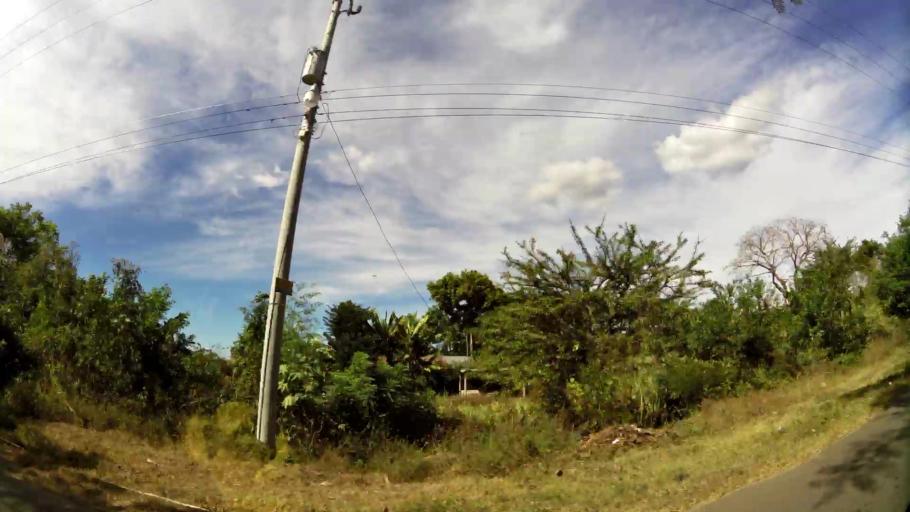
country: SV
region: San Salvador
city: Aguilares
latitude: 13.9644
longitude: -89.1171
